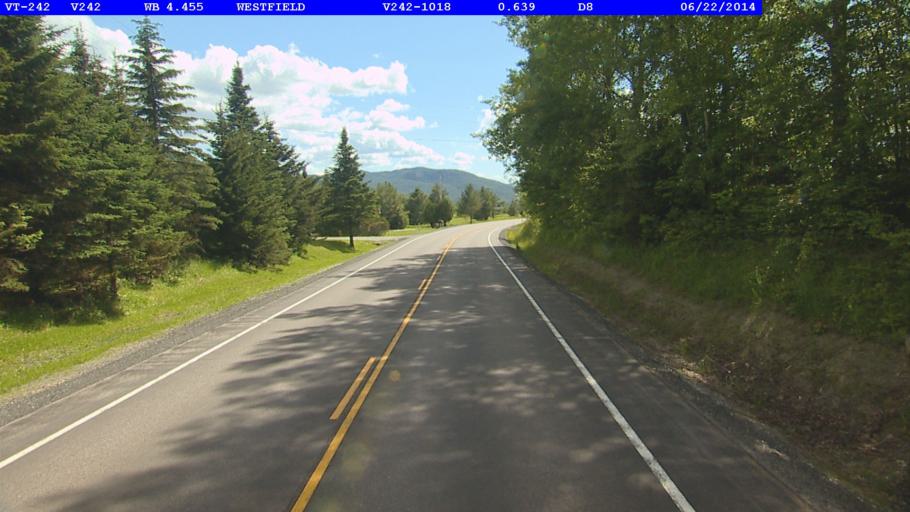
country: US
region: Vermont
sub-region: Franklin County
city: Richford
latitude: 44.8917
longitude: -72.5275
